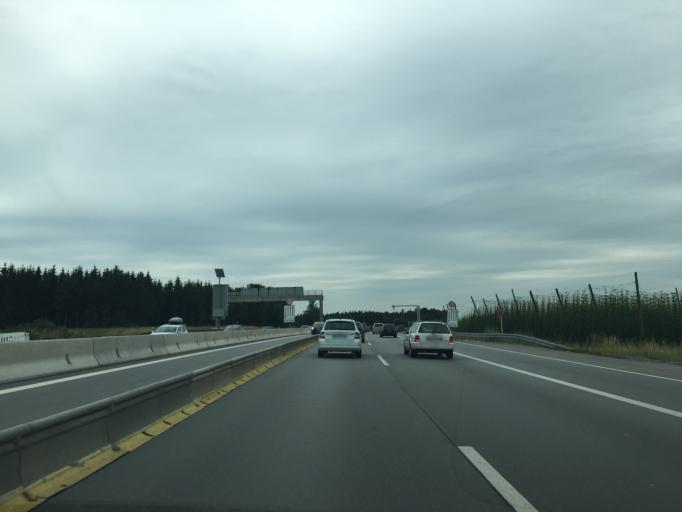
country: DE
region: Bavaria
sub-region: Upper Bavaria
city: Schweitenkirchen
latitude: 48.5226
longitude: 11.5840
